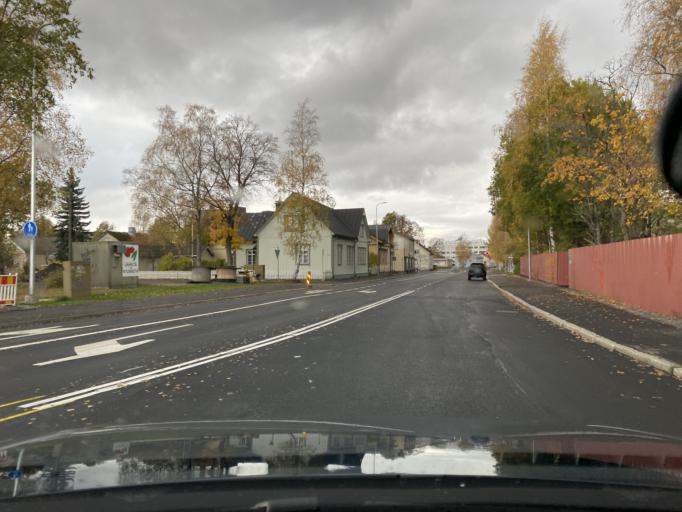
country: FI
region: Haeme
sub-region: Forssa
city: Forssa
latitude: 60.8096
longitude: 23.6284
